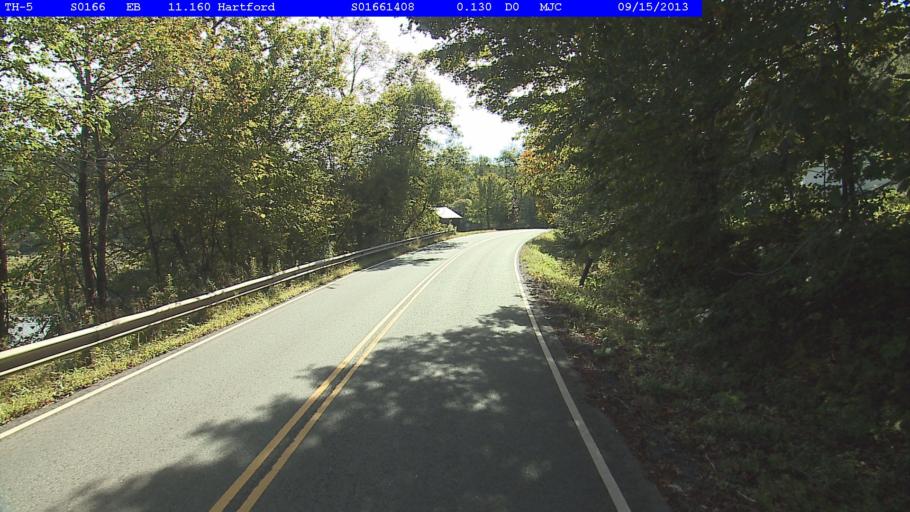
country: US
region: Vermont
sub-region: Windsor County
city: Wilder
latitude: 43.7208
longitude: -72.4240
